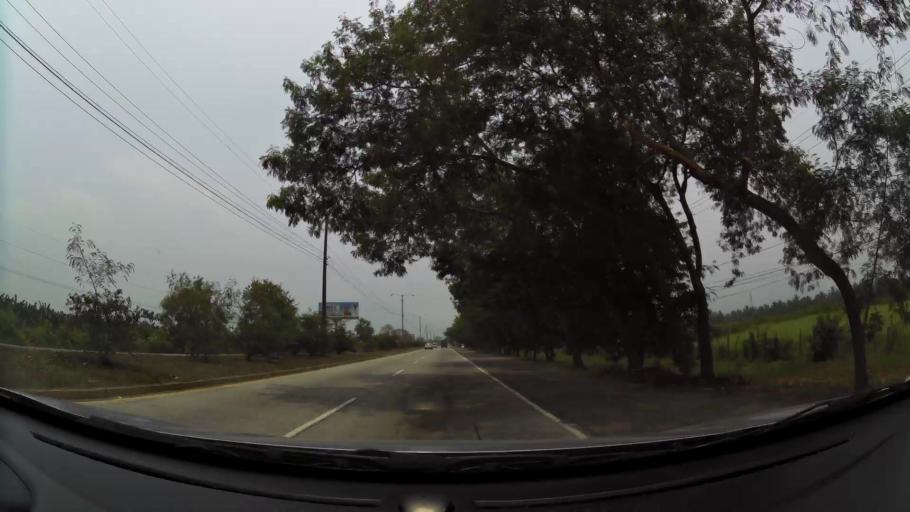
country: HN
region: Yoro
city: El Progreso
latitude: 15.4065
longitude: -87.8284
